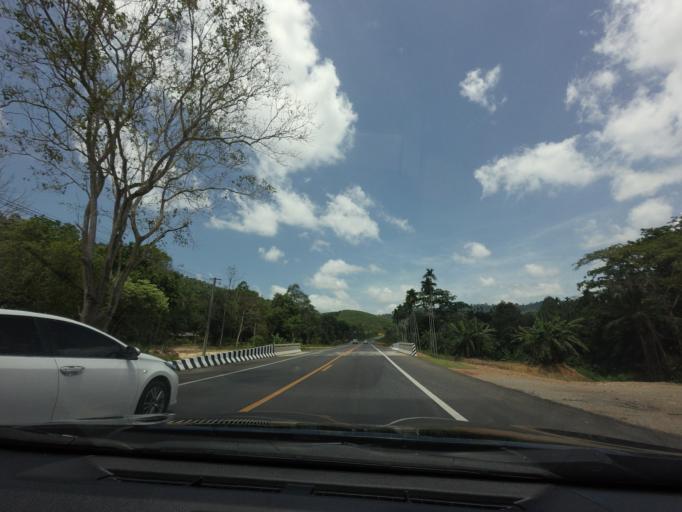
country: TH
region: Chumphon
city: Ban Nam Yuen
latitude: 9.9111
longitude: 98.9254
